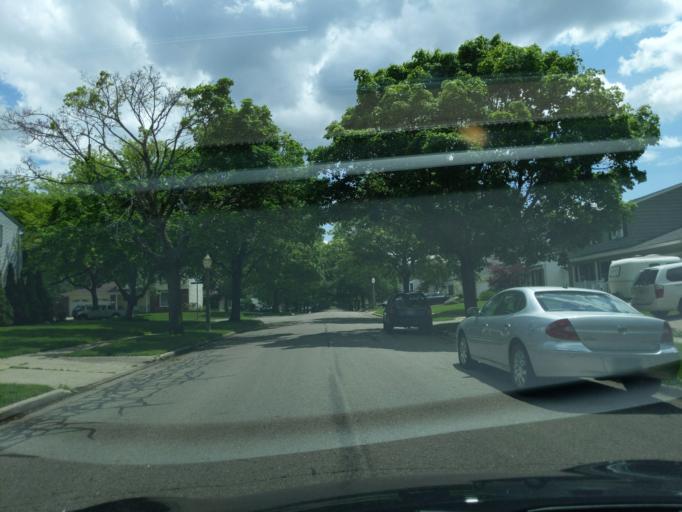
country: US
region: Michigan
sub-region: Ingham County
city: Lansing
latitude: 42.7528
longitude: -84.5216
